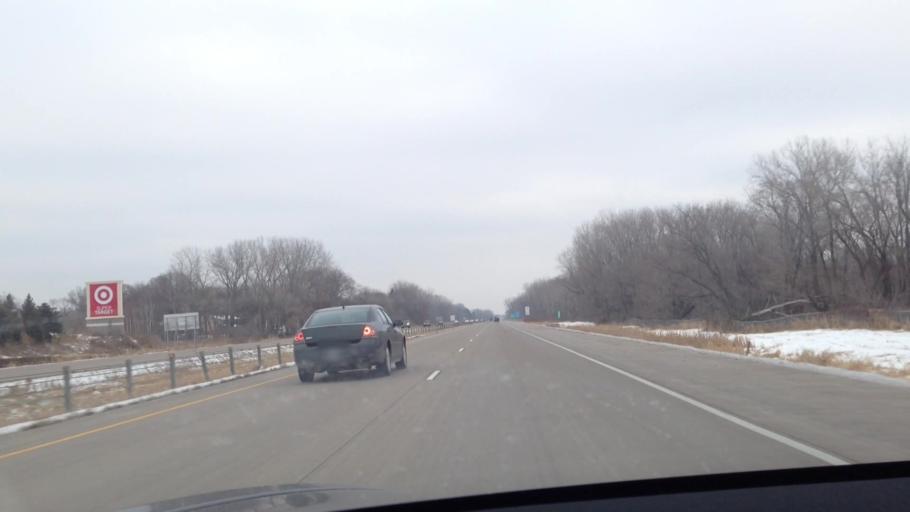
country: US
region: Minnesota
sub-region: Anoka County
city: Lino Lakes
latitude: 45.1827
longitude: -93.1051
